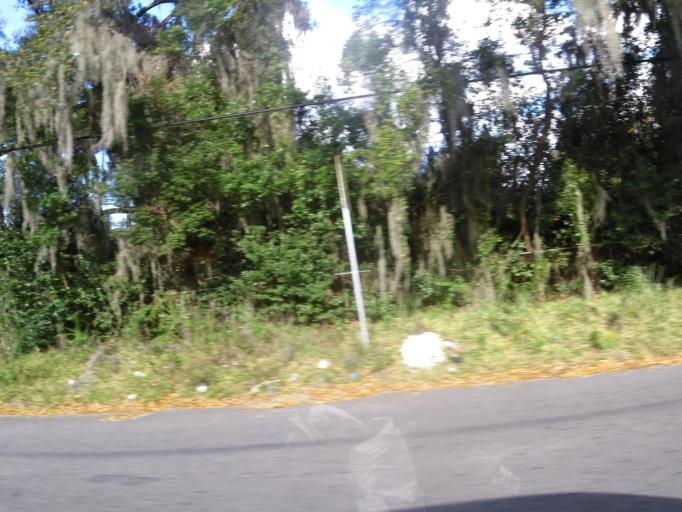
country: US
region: Florida
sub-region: Duval County
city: Jacksonville
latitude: 30.3812
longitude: -81.6607
